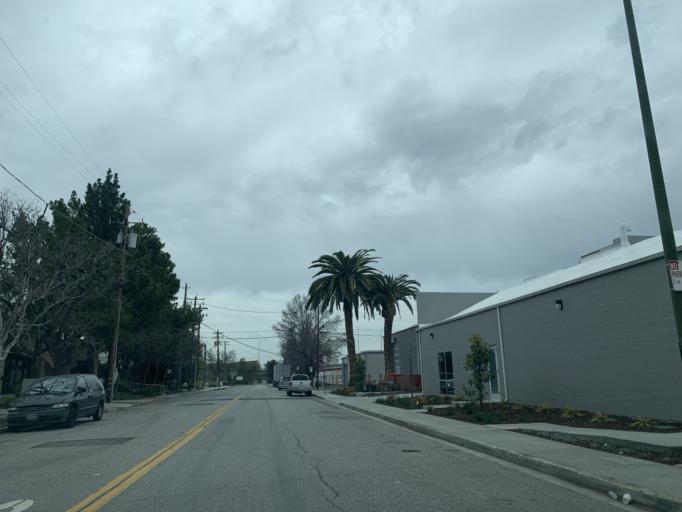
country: US
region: California
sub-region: Santa Clara County
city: Mountain View
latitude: 37.4086
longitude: -122.0755
